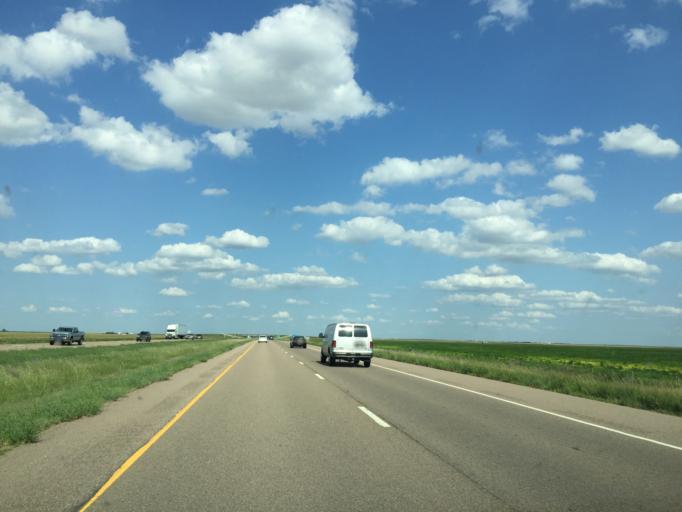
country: US
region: Kansas
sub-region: Gove County
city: Gove
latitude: 39.0971
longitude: -100.3848
